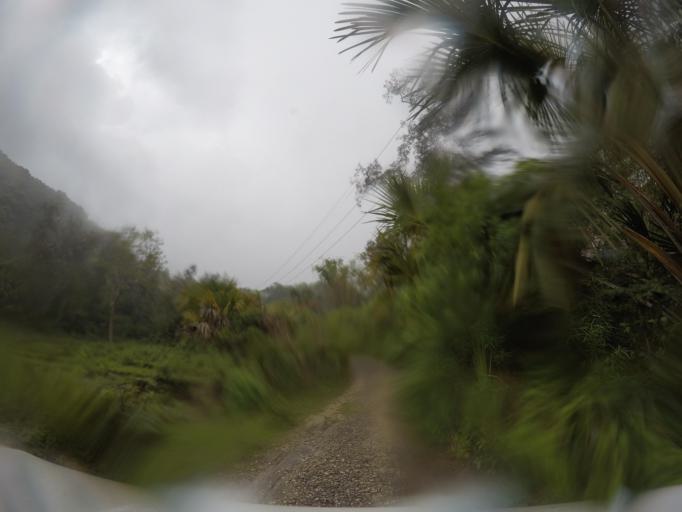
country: TL
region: Baucau
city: Venilale
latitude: -8.6422
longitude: 126.4346
